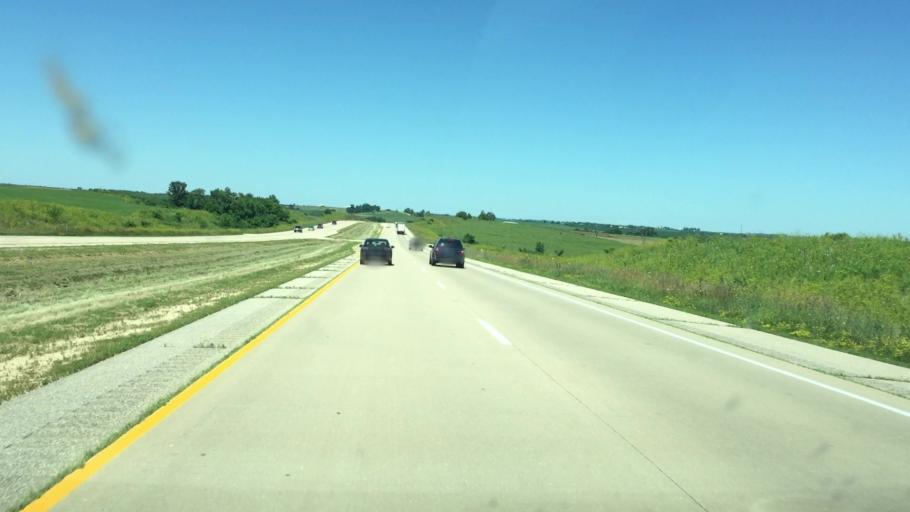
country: US
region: Wisconsin
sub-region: Iowa County
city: Mineral Point
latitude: 42.8003
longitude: -90.2771
